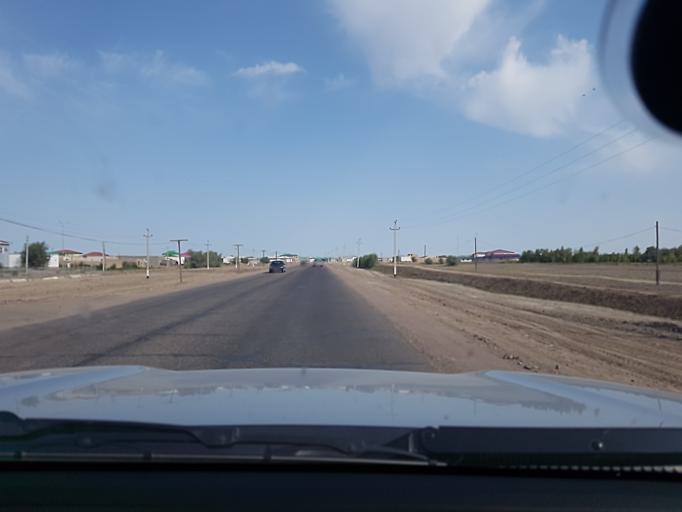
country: TM
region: Dasoguz
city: Dasoguz
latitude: 41.8071
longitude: 60.0057
